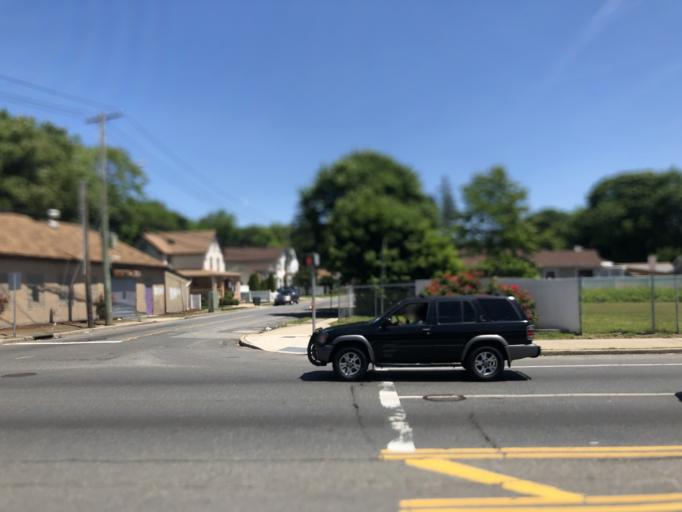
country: US
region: New York
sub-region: Nassau County
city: Roosevelt
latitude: 40.6859
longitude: -73.5936
